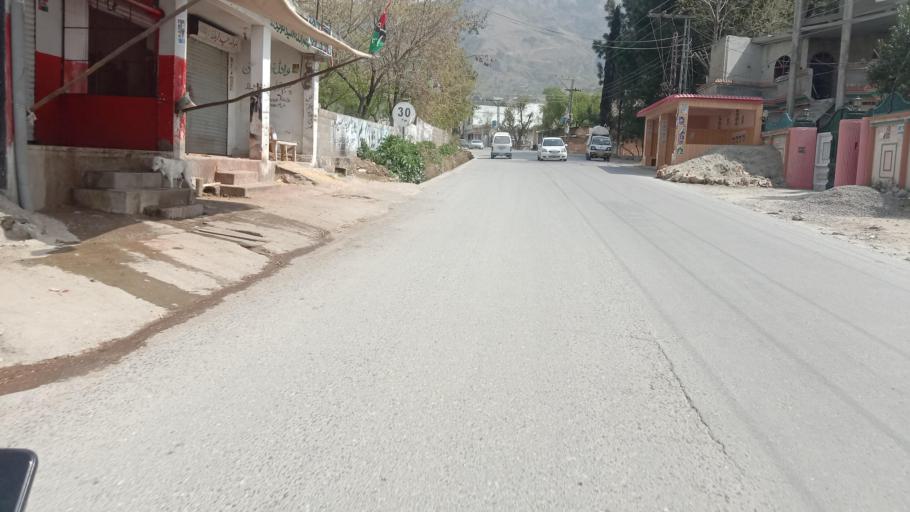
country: PK
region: Khyber Pakhtunkhwa
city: Abbottabad
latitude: 34.1389
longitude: 73.2765
